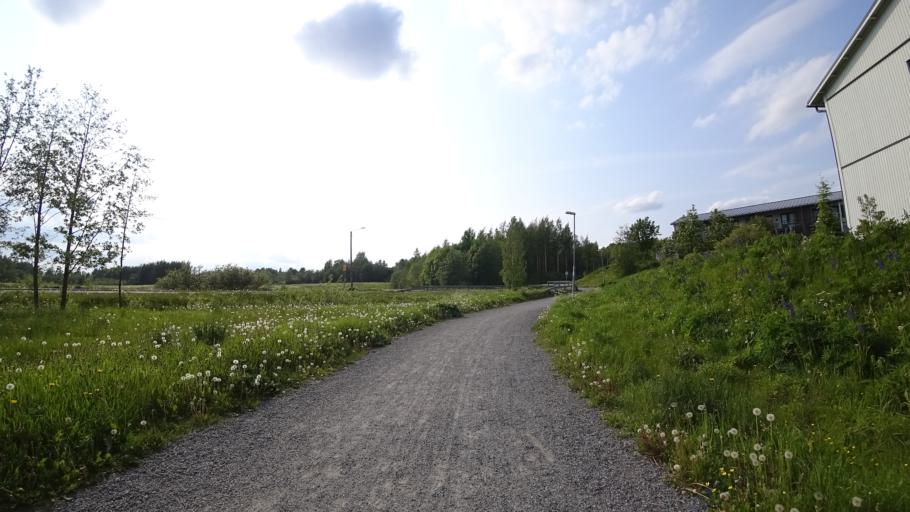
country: FI
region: Pirkanmaa
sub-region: Tampere
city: Pirkkala
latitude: 61.5037
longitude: 23.6846
